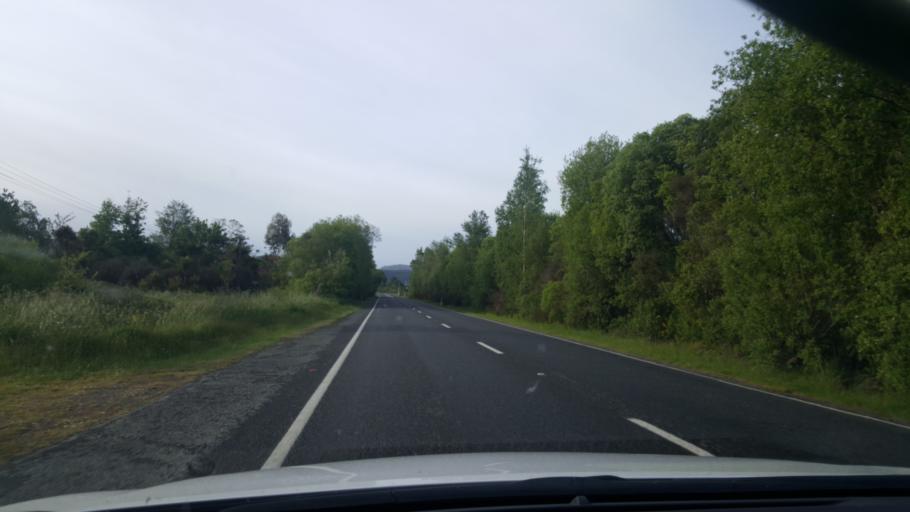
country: NZ
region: Waikato
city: Turangi
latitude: -38.9678
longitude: 175.7681
